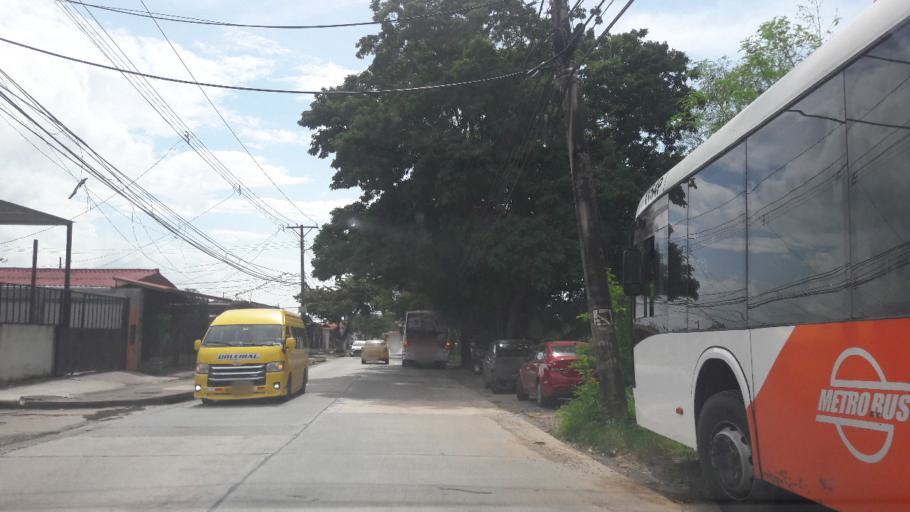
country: PA
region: Panama
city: Tocumen
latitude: 9.0603
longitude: -79.4202
